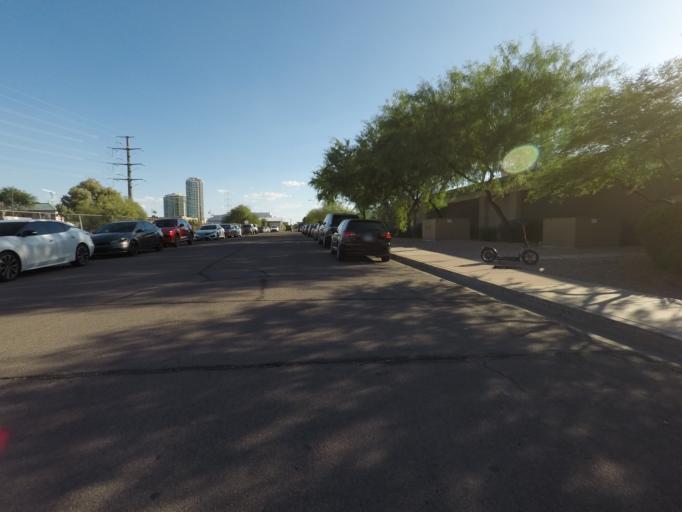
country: US
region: Arizona
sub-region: Maricopa County
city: Tempe Junction
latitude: 33.4306
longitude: -111.9443
